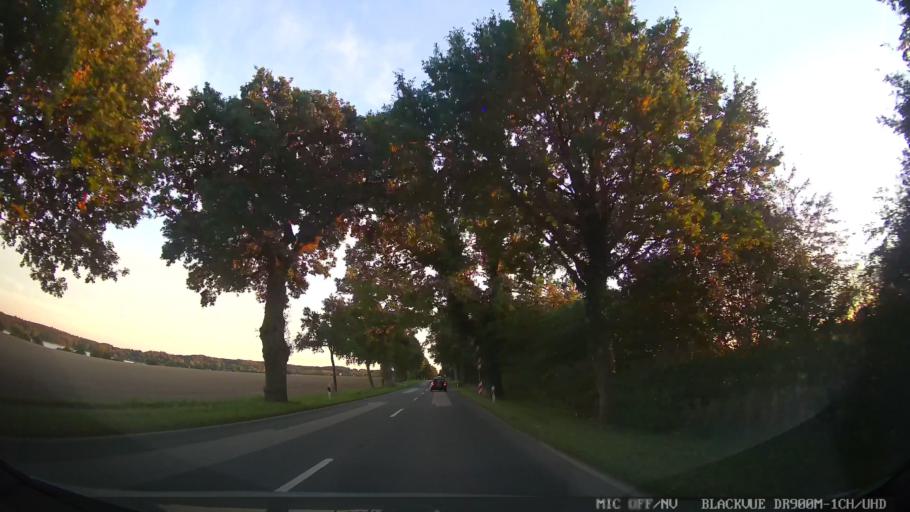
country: DE
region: Schleswig-Holstein
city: Susel
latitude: 54.0352
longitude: 10.6816
